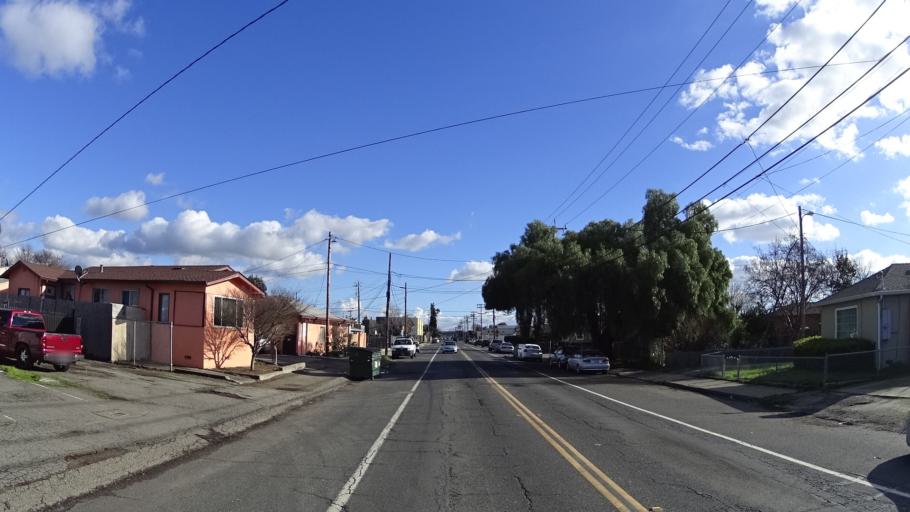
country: US
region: California
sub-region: Alameda County
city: Cherryland
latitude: 37.6723
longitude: -122.1051
